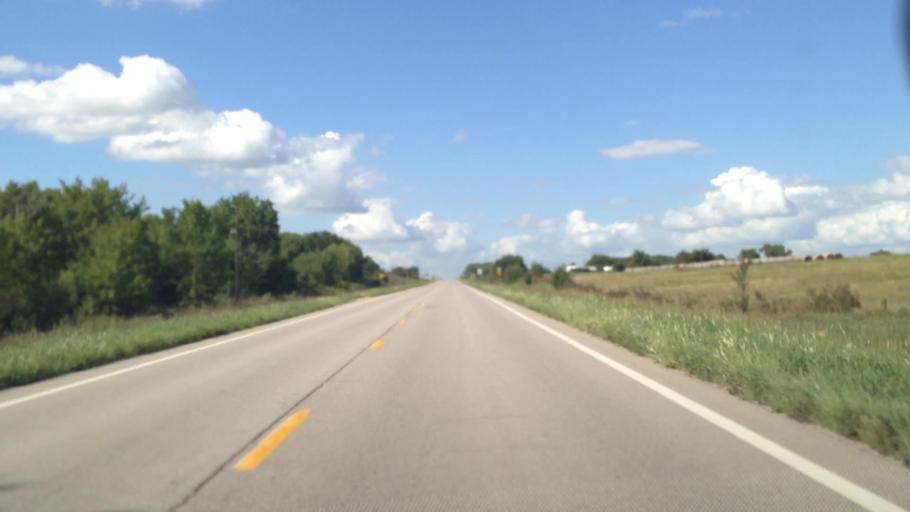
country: US
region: Kansas
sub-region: Neosho County
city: Erie
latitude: 37.7148
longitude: -95.1607
